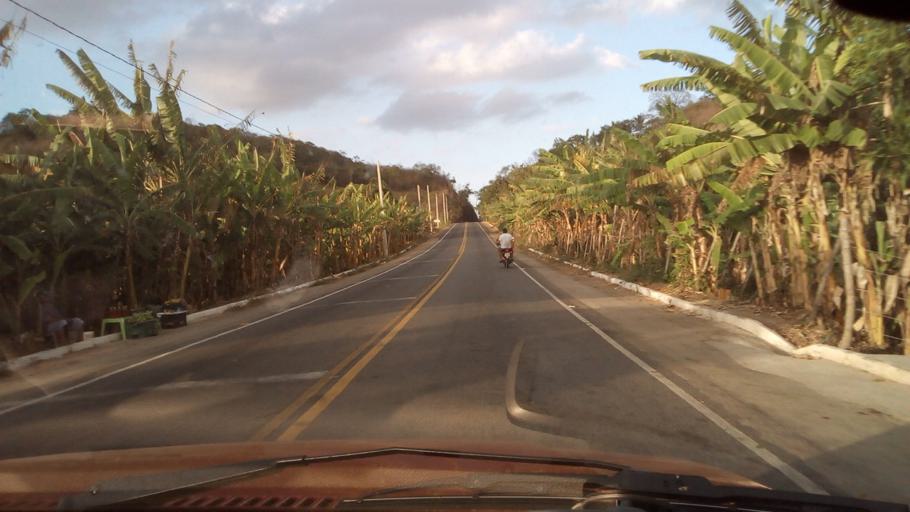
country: BR
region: Paraiba
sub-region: Bananeiras
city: Solanea
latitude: -6.7501
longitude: -35.5652
